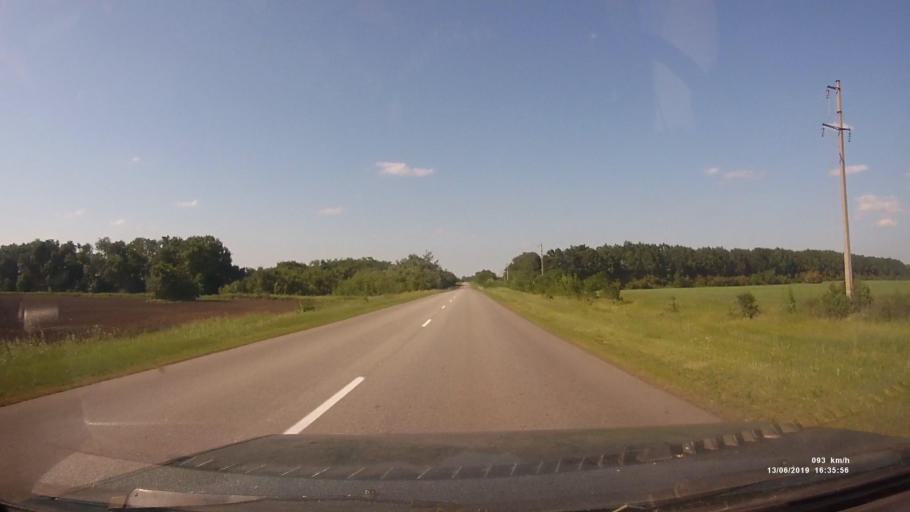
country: RU
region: Rostov
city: Kazanskaya
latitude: 49.8885
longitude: 41.3020
